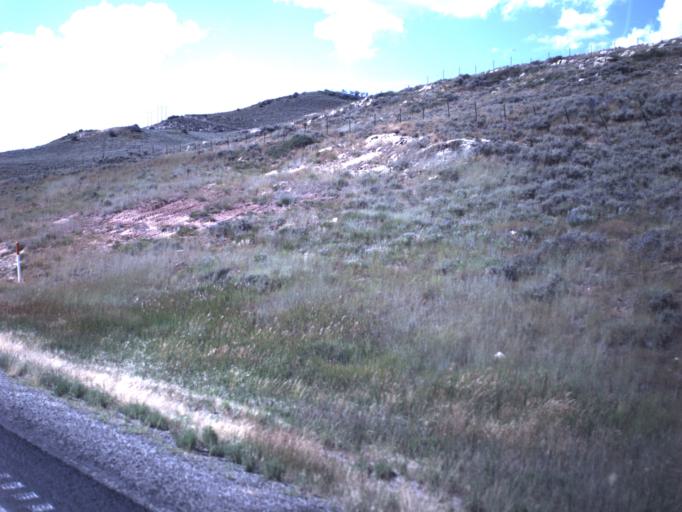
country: US
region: Utah
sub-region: Wasatch County
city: Heber
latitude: 40.1867
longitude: -111.0650
